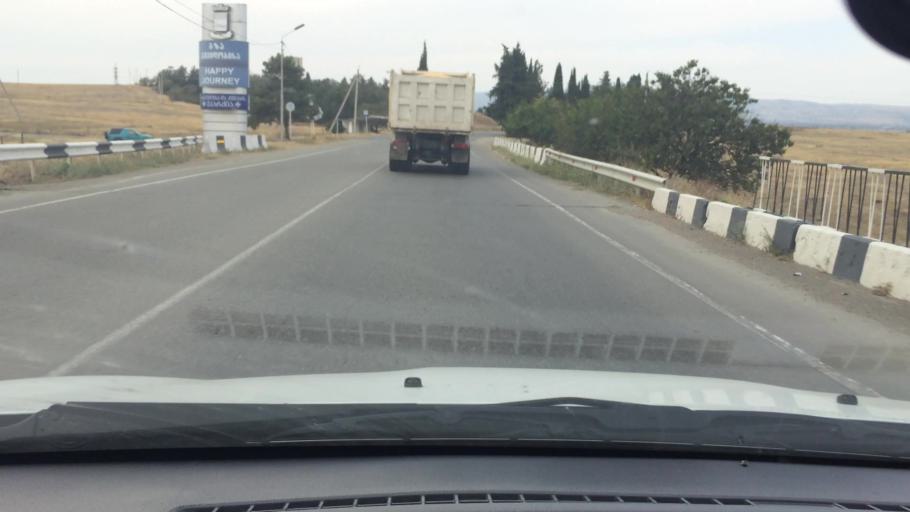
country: GE
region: Kvemo Kartli
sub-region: Marneuli
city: Marneuli
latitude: 41.5211
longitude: 44.7798
